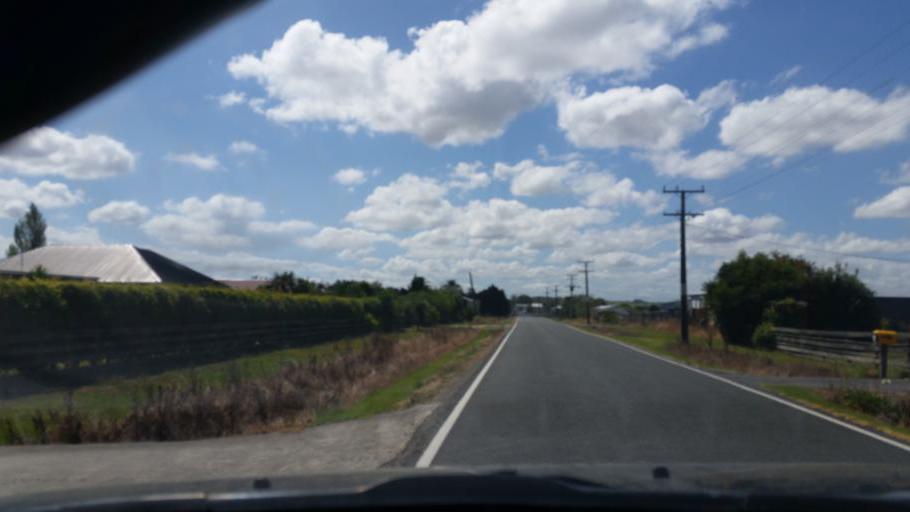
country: NZ
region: Northland
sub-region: Kaipara District
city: Dargaville
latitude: -35.9442
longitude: 173.8582
